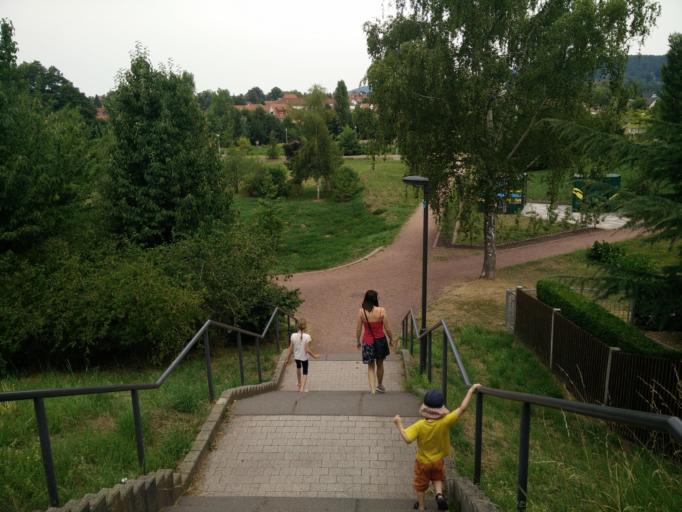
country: DE
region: Thuringia
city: Bad Liebenstein
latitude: 50.8129
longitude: 10.3494
